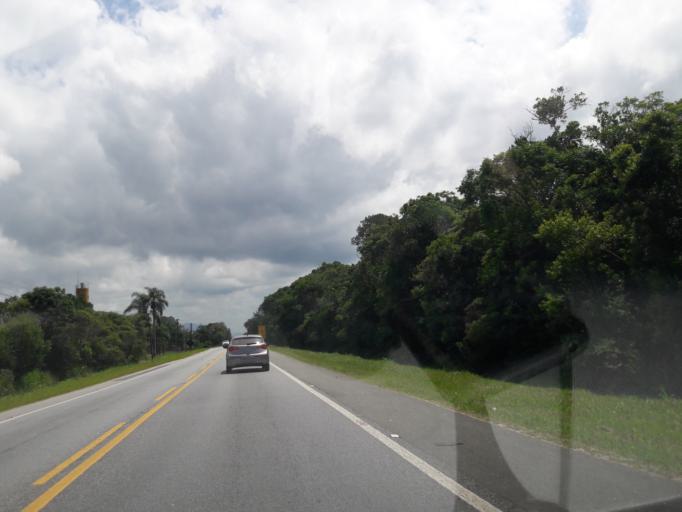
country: BR
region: Parana
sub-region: Pontal Do Parana
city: Pontal do Parana
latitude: -25.6764
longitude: -48.5064
